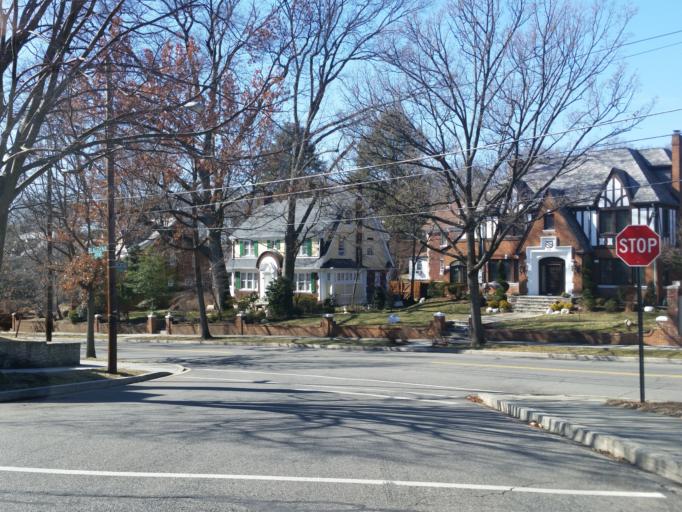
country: US
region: Maryland
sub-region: Montgomery County
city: Takoma Park
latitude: 38.9483
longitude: -77.0389
